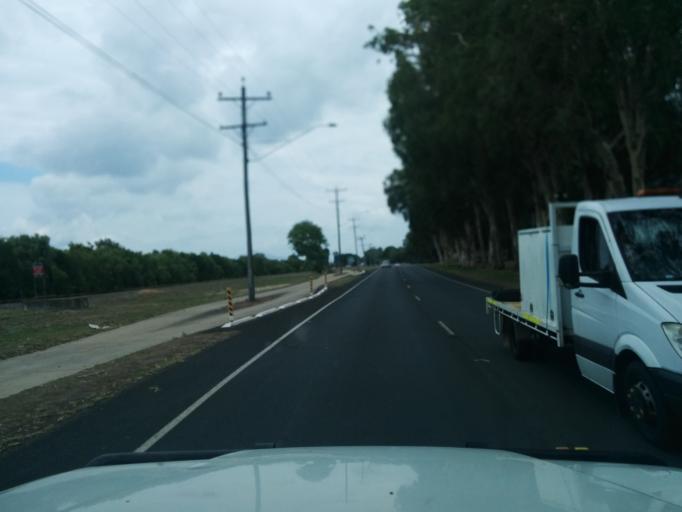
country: AU
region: Queensland
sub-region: Cairns
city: Cairns
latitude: -16.8885
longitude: 145.7504
